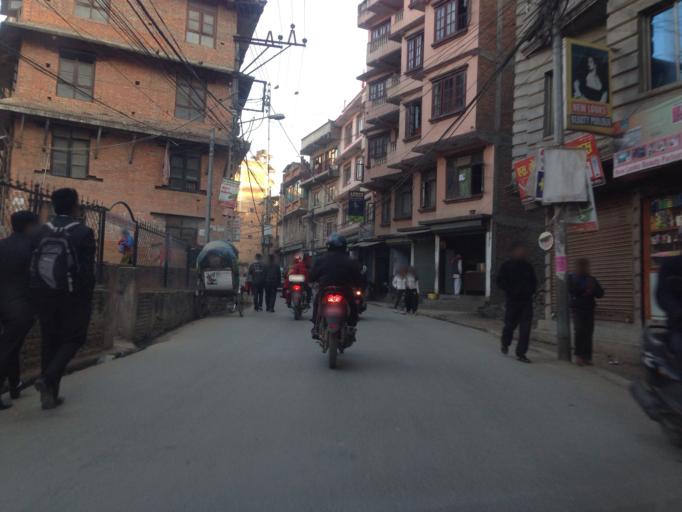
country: NP
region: Central Region
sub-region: Bagmati Zone
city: Kathmandu
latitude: 27.7121
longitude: 85.3057
